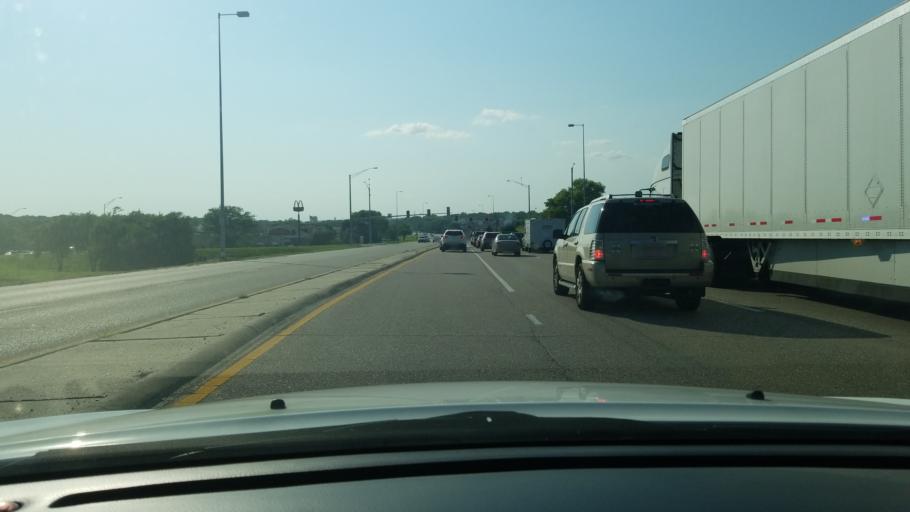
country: US
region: Nebraska
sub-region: Lancaster County
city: Lincoln
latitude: 40.7536
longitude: -96.6390
